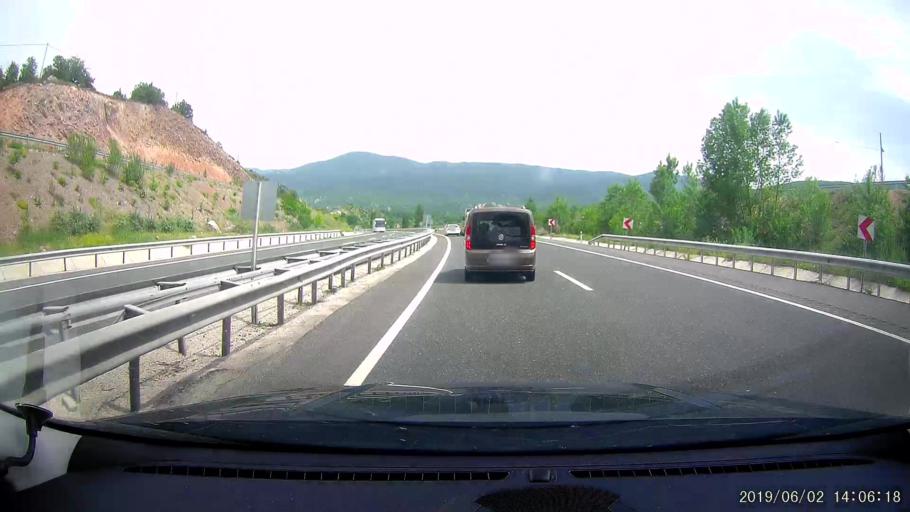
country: TR
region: Cankiri
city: Ilgaz
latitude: 40.8904
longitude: 33.6784
